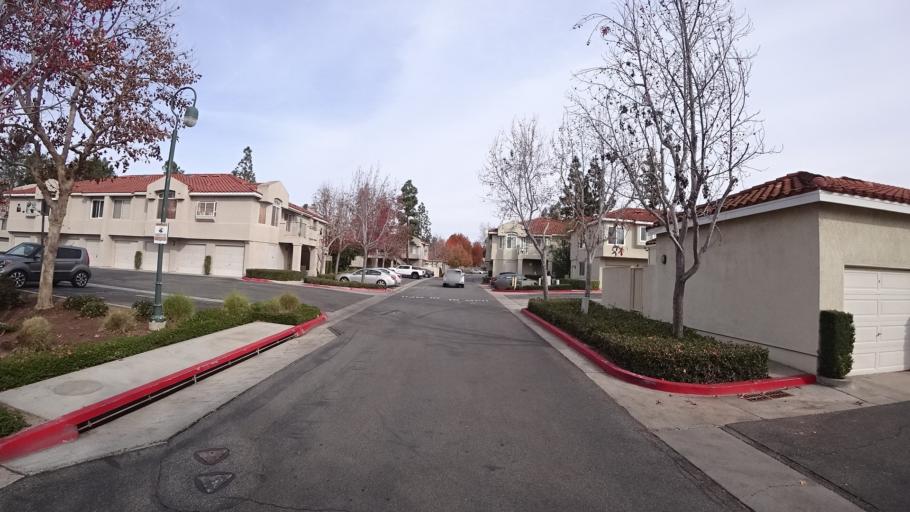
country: US
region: California
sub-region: Orange County
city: Laguna Woods
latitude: 33.6000
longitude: -117.7451
